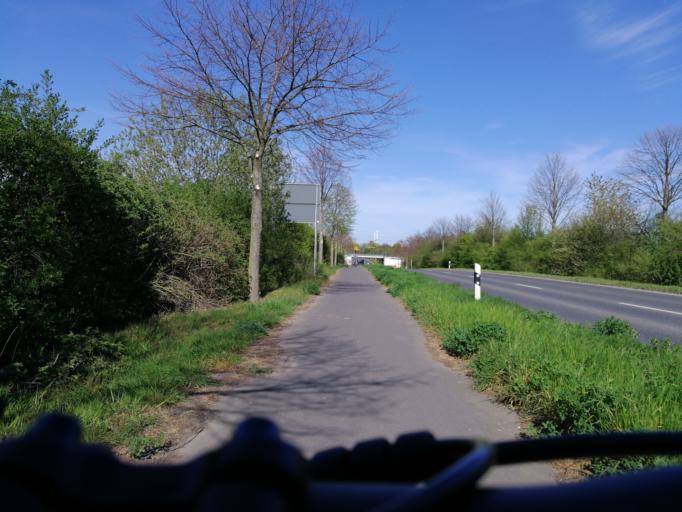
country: DE
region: North Rhine-Westphalia
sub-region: Regierungsbezirk Dusseldorf
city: Dormagen
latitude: 51.1379
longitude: 6.7591
